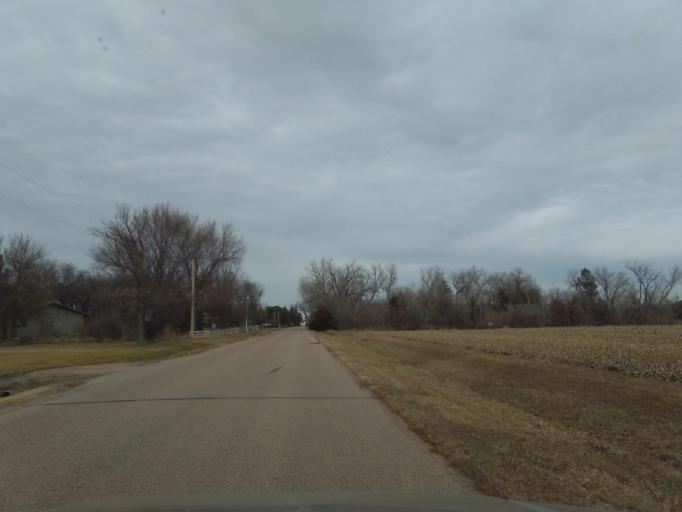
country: US
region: Nebraska
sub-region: Hall County
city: Grand Island
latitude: 40.7733
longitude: -98.4119
